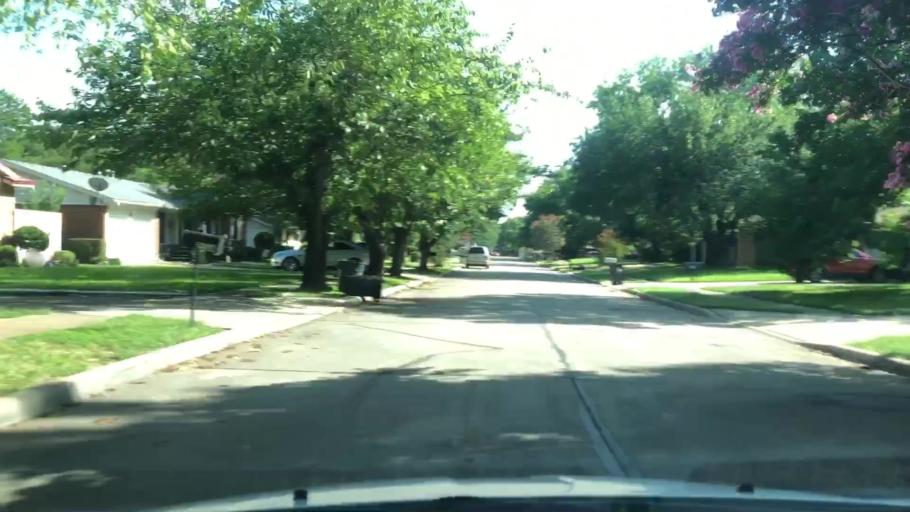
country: US
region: Texas
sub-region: Ellis County
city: Ennis
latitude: 32.3479
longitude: -96.6480
